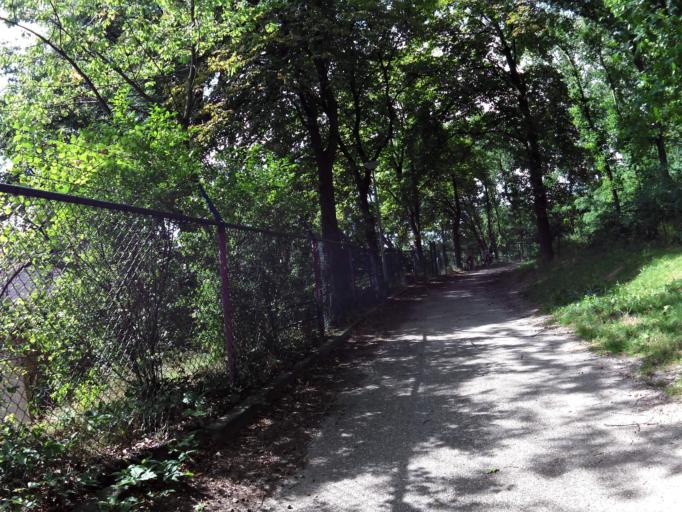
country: NL
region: Limburg
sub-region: Gemeente Heerlen
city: Heerlen
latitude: 50.9108
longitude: 6.0177
